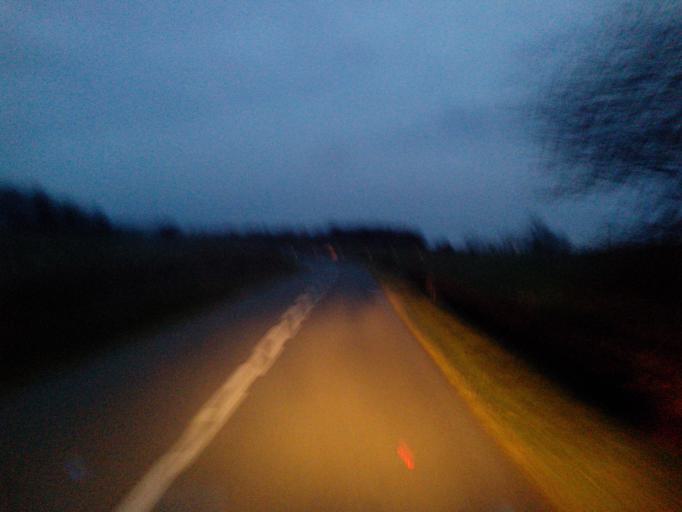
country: FR
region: Languedoc-Roussillon
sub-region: Departement de l'Aude
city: Villeneuve-la-Comptal
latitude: 43.2814
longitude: 1.8509
